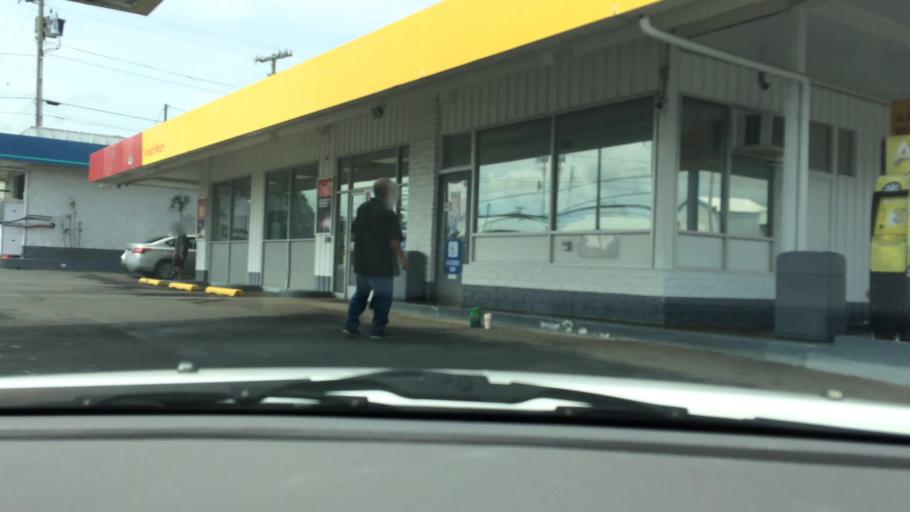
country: US
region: Hawaii
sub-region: Hawaii County
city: Hilo
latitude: 19.7124
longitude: -155.0774
